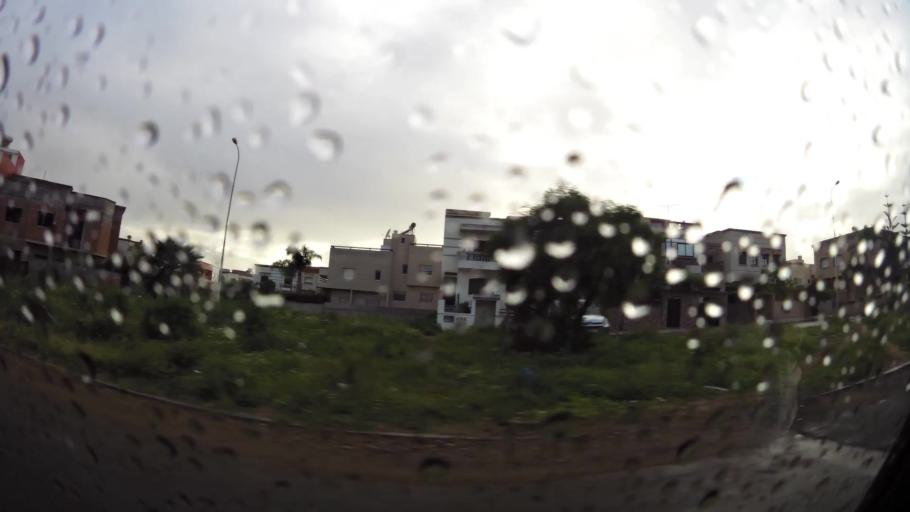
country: MA
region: Doukkala-Abda
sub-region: El-Jadida
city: El Jadida
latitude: 33.2273
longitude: -8.4966
